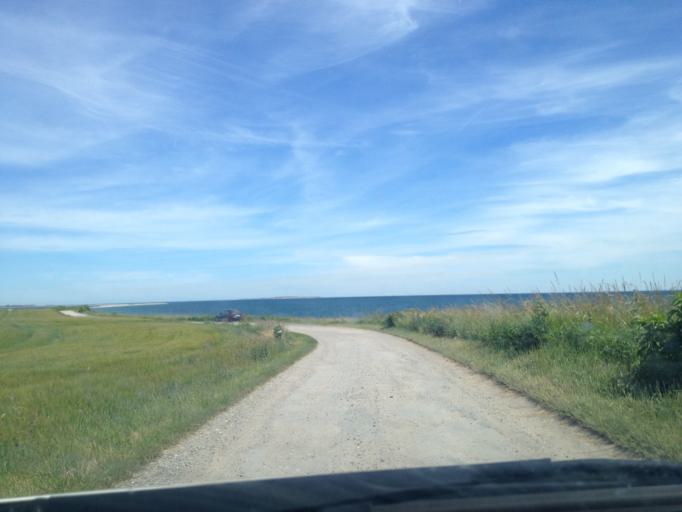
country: DK
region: Central Jutland
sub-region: Samso Kommune
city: Tranebjerg
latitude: 55.8789
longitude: 10.6762
